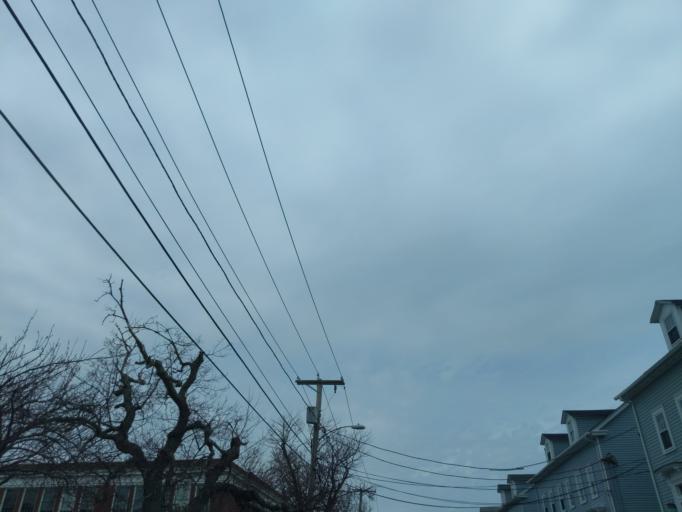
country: US
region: Massachusetts
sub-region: Essex County
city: Rockport
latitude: 42.6574
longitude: -70.6175
